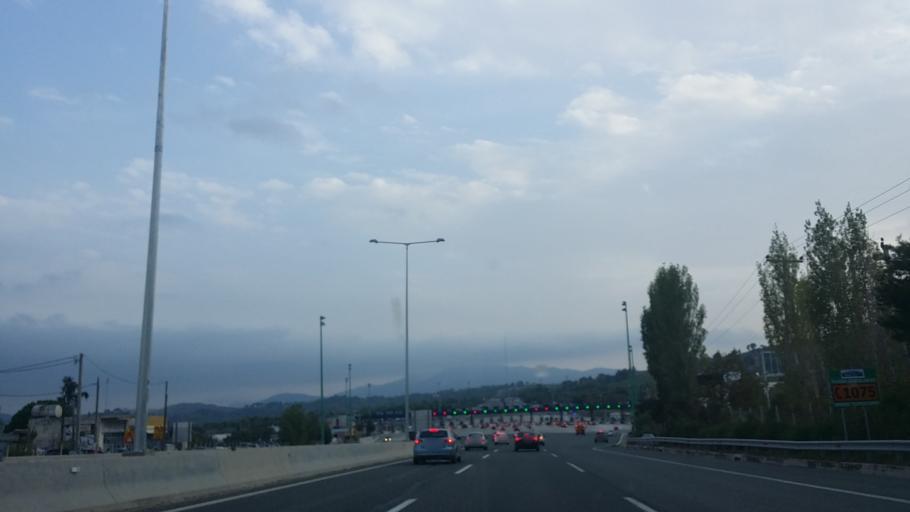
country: GR
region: Attica
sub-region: Nomarchia Anatolikis Attikis
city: Afidnes
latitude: 38.1801
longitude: 23.8533
